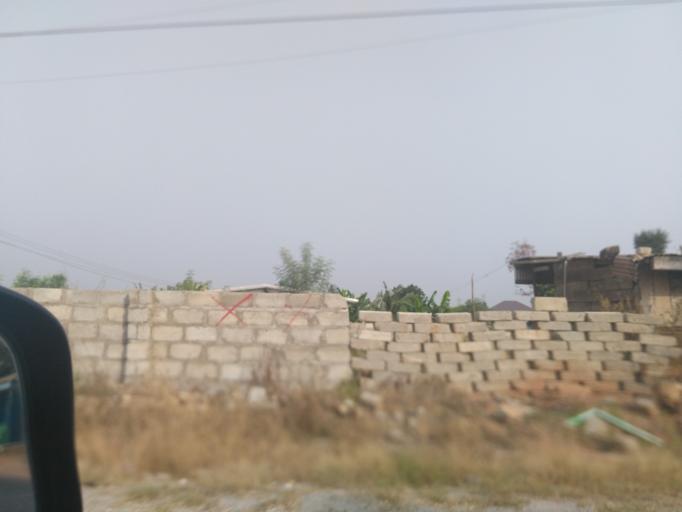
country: GH
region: Greater Accra
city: Accra
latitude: 5.6074
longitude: -0.1994
